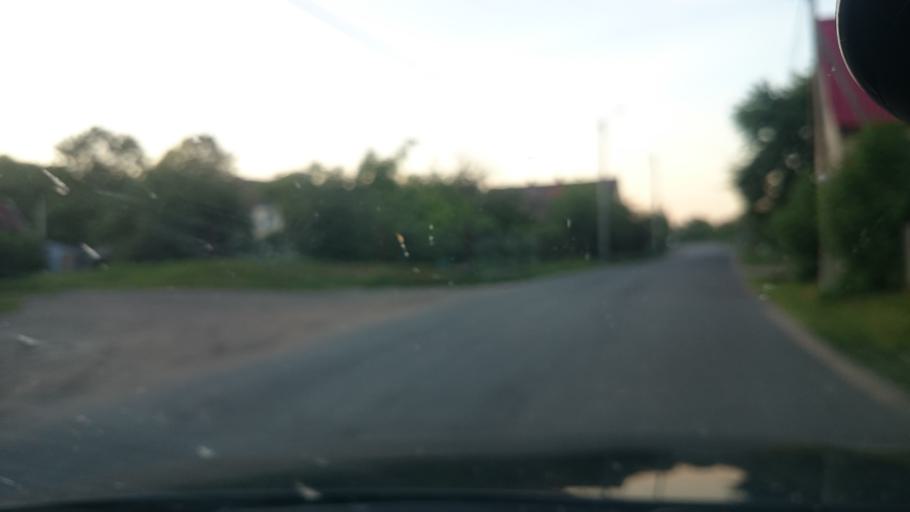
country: PL
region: Lower Silesian Voivodeship
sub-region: Powiat zabkowicki
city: Kamieniec Zabkowicki
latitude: 50.4946
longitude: 16.8291
